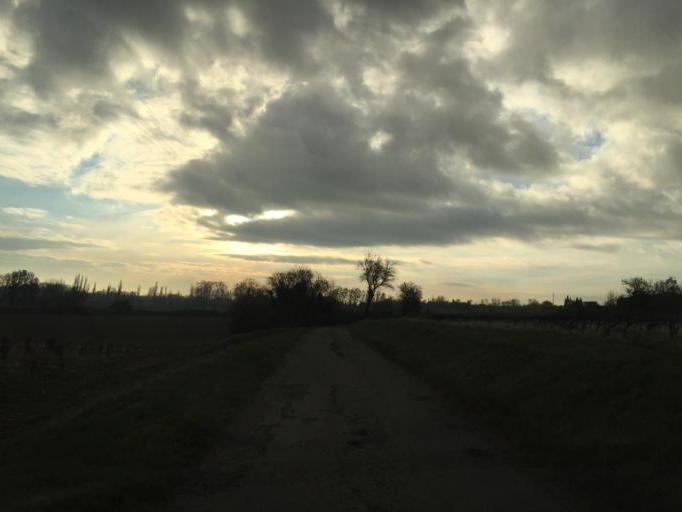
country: FR
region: Provence-Alpes-Cote d'Azur
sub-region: Departement du Vaucluse
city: Courthezon
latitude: 44.1058
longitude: 4.8781
